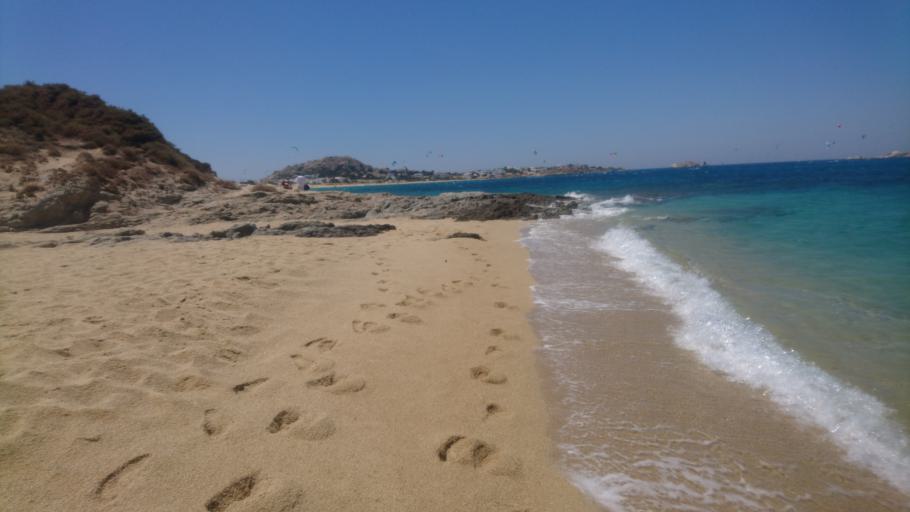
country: GR
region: South Aegean
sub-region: Nomos Kykladon
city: Naxos
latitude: 37.0322
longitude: 25.3730
